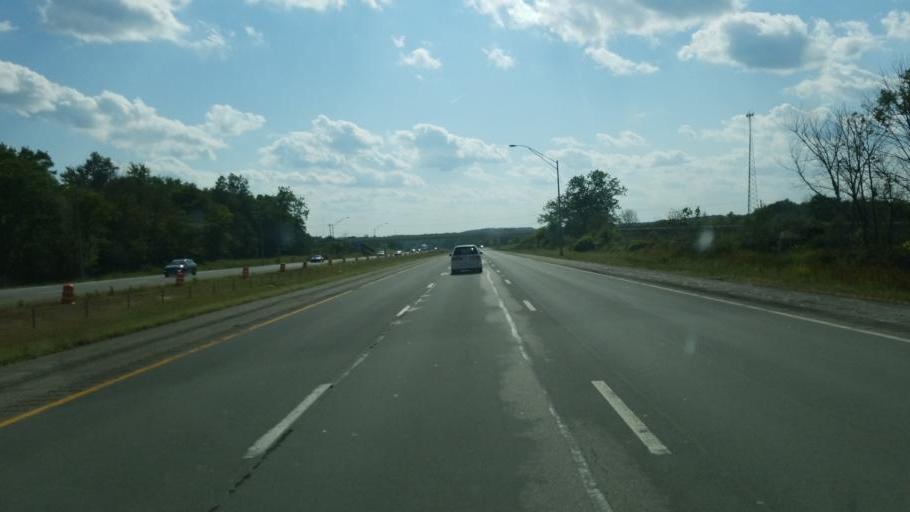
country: US
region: Ohio
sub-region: Wayne County
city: West Salem
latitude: 40.9370
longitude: -82.1062
